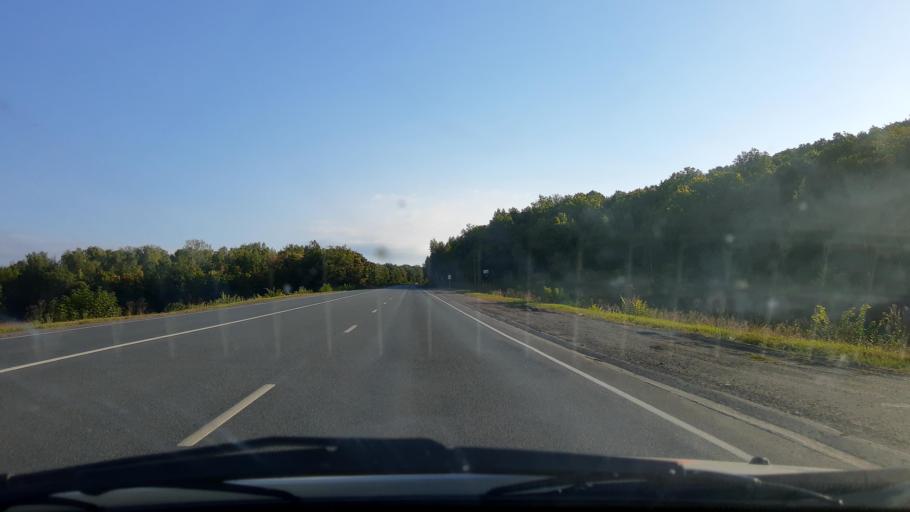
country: RU
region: Bashkortostan
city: Oktyabr'skiy
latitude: 54.4353
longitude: 53.4984
